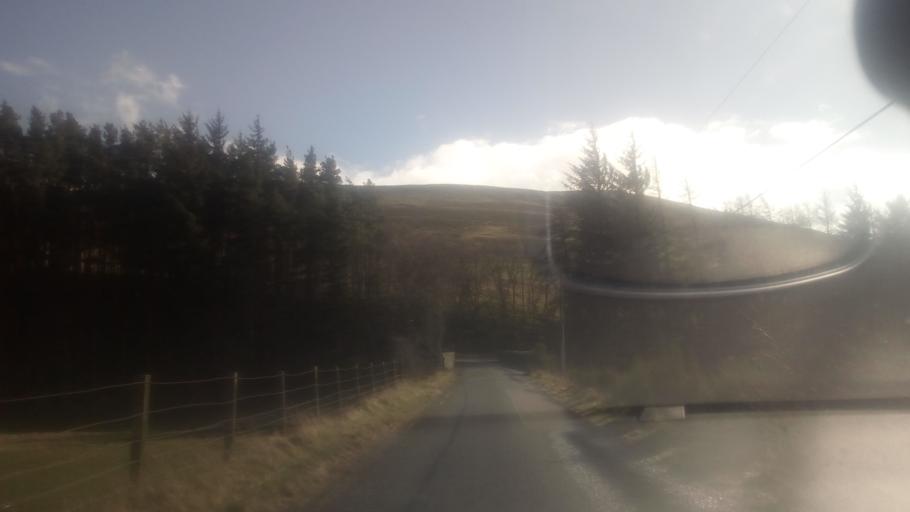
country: GB
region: Scotland
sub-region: The Scottish Borders
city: Innerleithen
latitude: 55.5118
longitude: -3.0968
